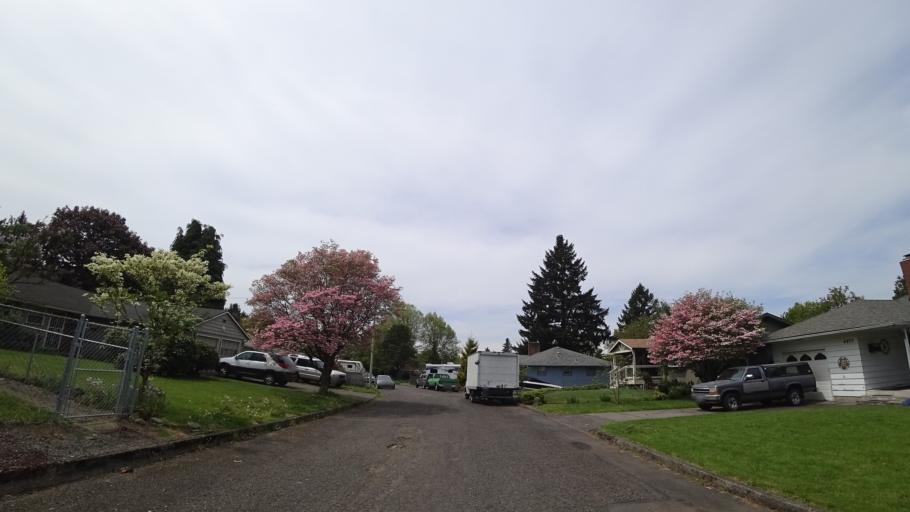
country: US
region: Oregon
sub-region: Clackamas County
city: Milwaukie
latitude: 45.4524
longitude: -122.6114
